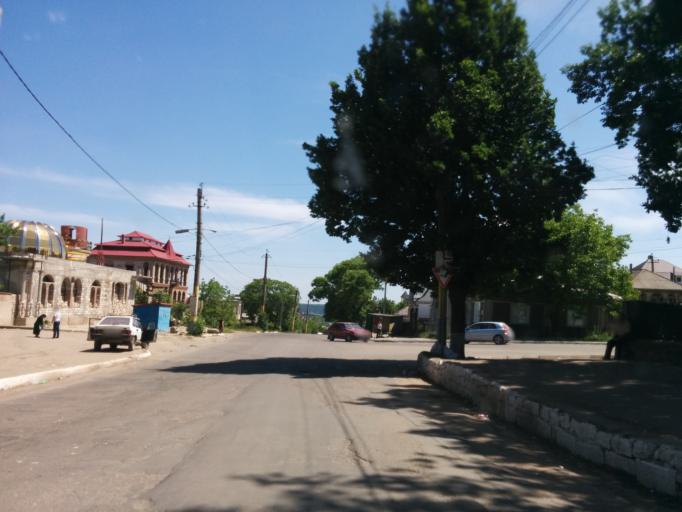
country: MD
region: Raionul Soroca
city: Soroca
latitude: 48.1612
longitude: 28.2914
